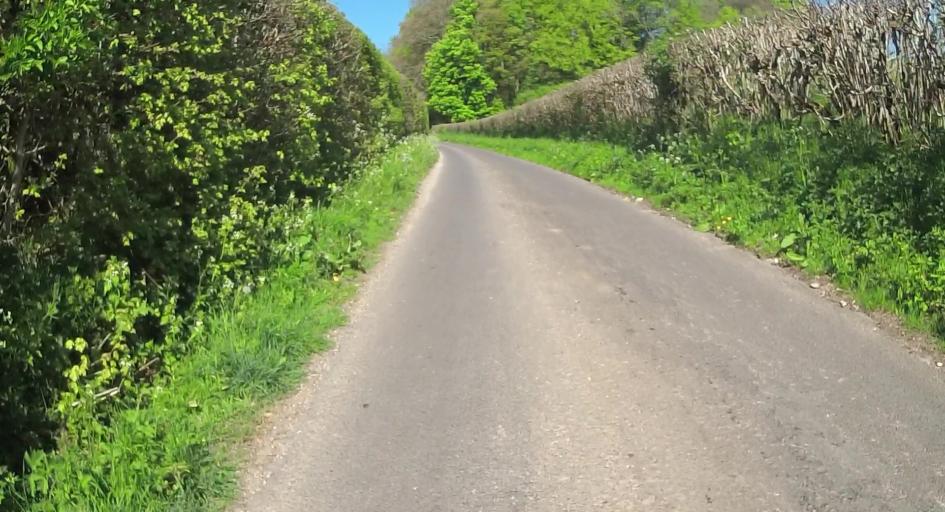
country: GB
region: England
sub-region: Hampshire
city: Alton
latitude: 51.1661
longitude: -1.0217
